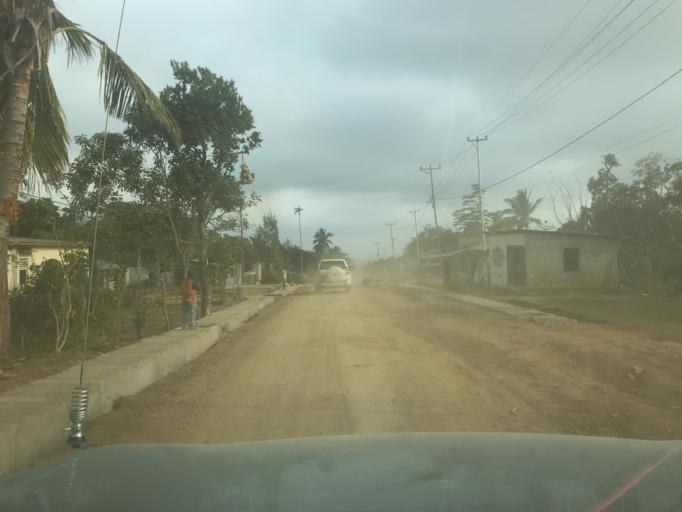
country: TL
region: Ainaro
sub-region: Ainaro
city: Ainaro
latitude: -9.0026
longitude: 125.5009
